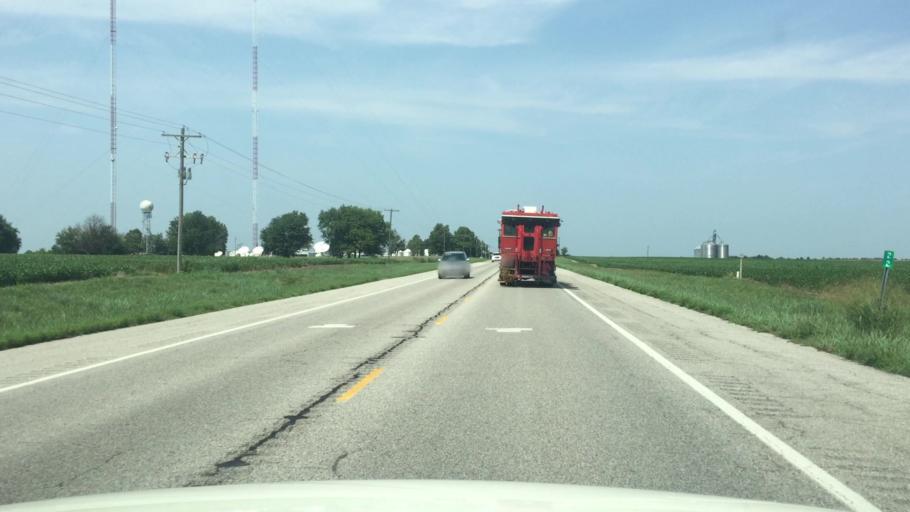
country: US
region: Missouri
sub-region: Jasper County
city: Carl Junction
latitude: 37.2168
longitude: -94.7048
